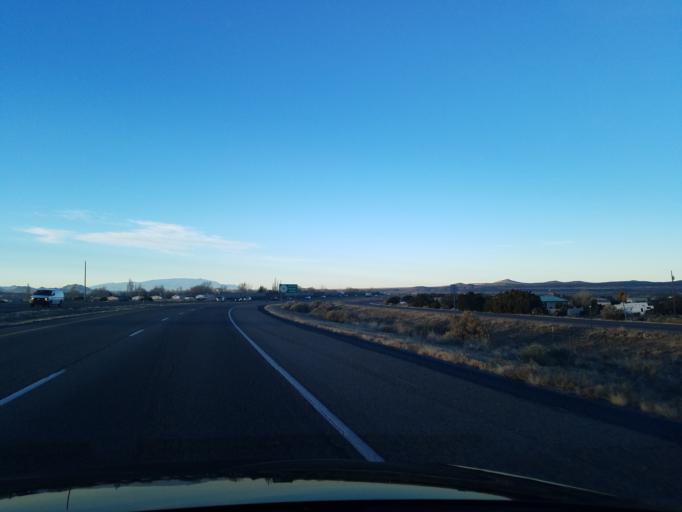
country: US
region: New Mexico
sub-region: Santa Fe County
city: Agua Fria
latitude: 35.6544
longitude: -106.0411
